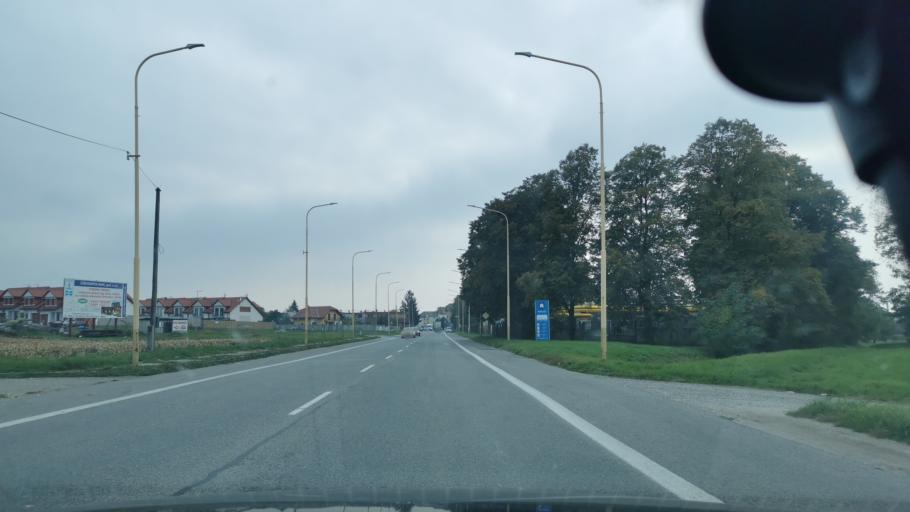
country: SK
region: Trnavsky
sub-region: Okres Skalica
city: Holic
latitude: 48.8225
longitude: 17.1650
